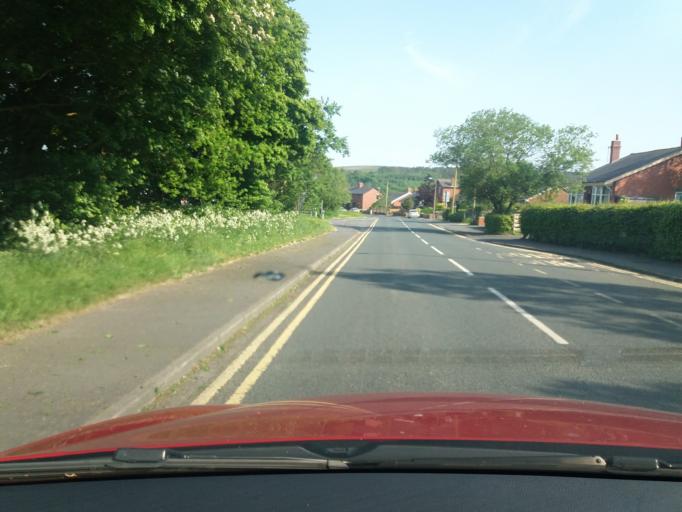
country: GB
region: England
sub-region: Lancashire
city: Chorley
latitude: 53.6898
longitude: -2.5746
